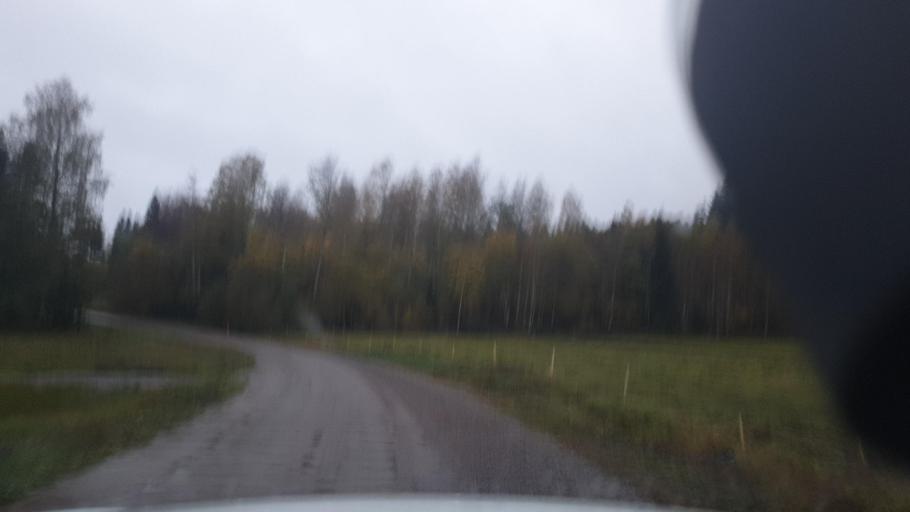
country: SE
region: Vaermland
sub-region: Eda Kommun
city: Amotfors
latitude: 59.8258
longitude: 12.4443
